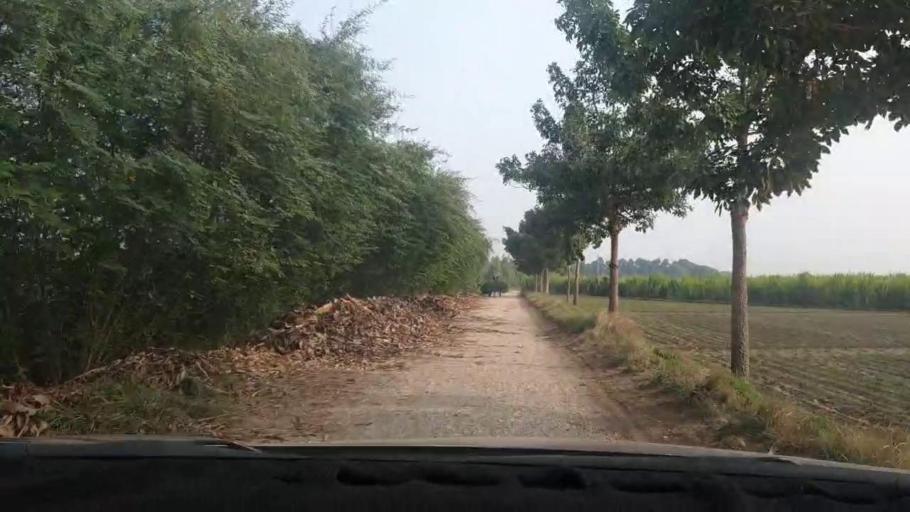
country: PK
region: Sindh
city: Matiari
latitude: 25.5811
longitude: 68.5160
